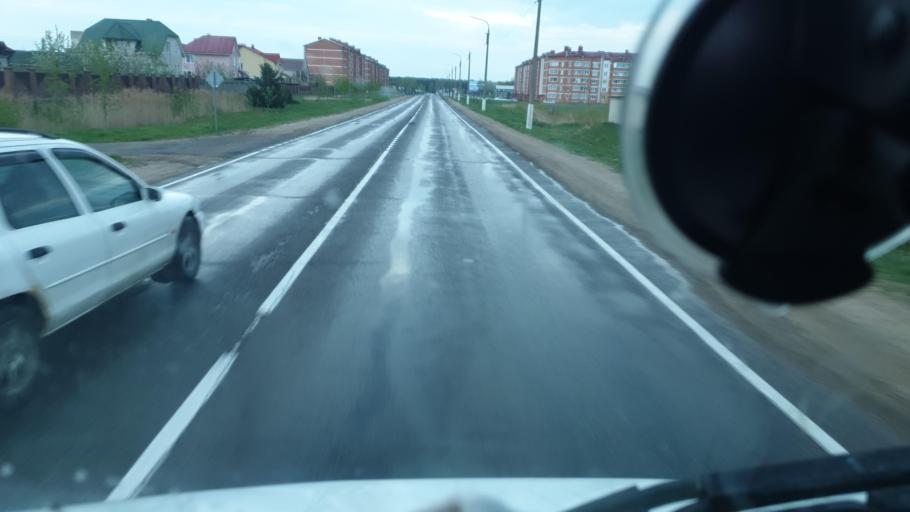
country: BY
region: Vitebsk
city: Lyepyel'
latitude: 54.8808
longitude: 28.7130
